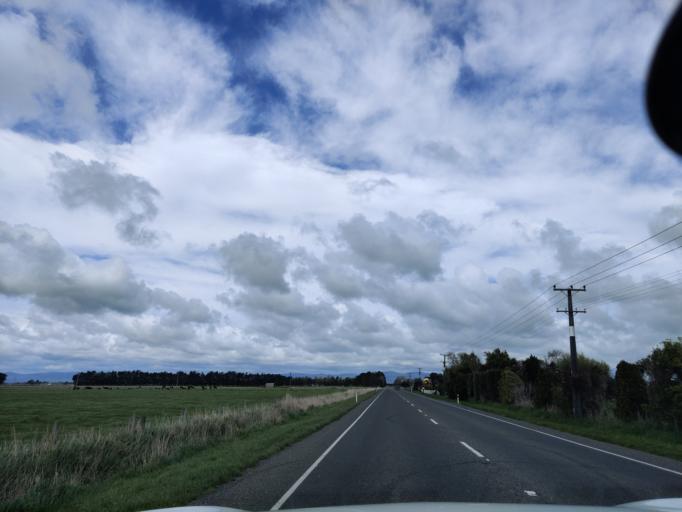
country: NZ
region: Manawatu-Wanganui
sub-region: Palmerston North City
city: Palmerston North
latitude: -40.3208
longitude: 175.4998
